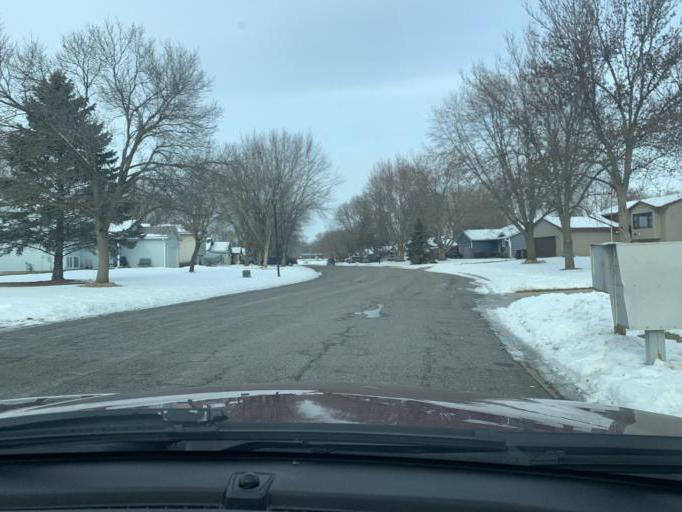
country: US
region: Minnesota
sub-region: Washington County
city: Saint Paul Park
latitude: 44.8307
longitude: -92.9865
